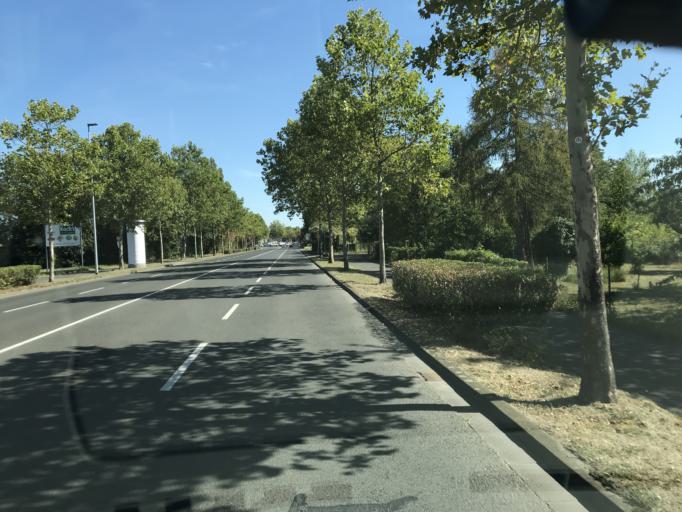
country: DE
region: Rheinland-Pfalz
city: Mainz
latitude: 50.0211
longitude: 8.2844
